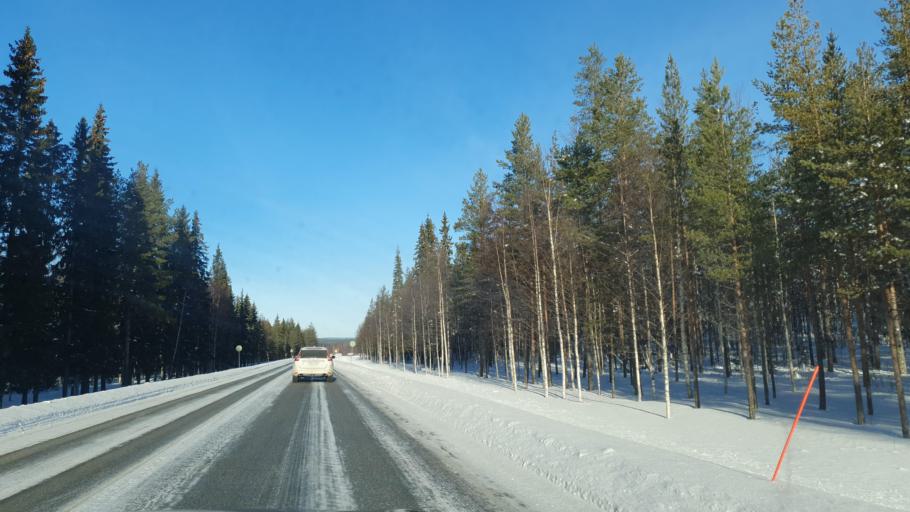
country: SE
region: Norrbotten
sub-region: Overtornea Kommun
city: OEvertornea
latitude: 66.4877
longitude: 23.7409
